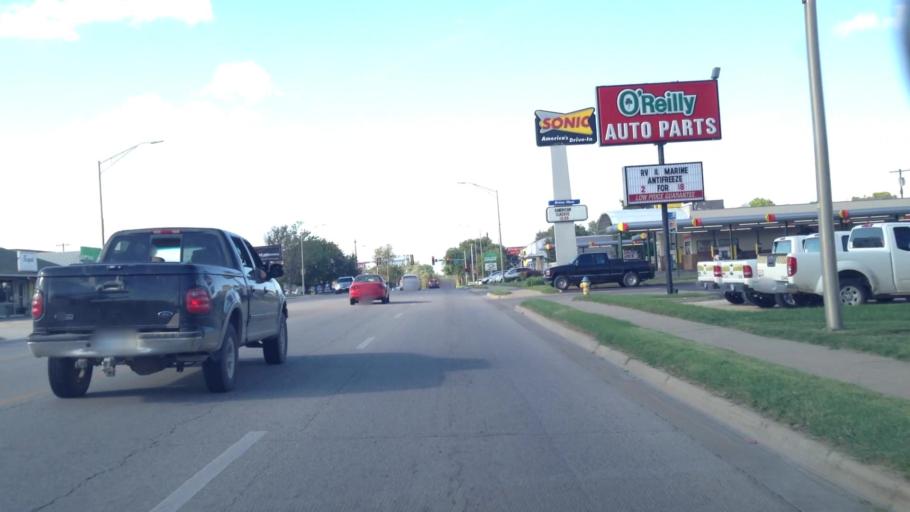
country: US
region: Kansas
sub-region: Franklin County
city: Ottawa
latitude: 38.5920
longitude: -95.2687
